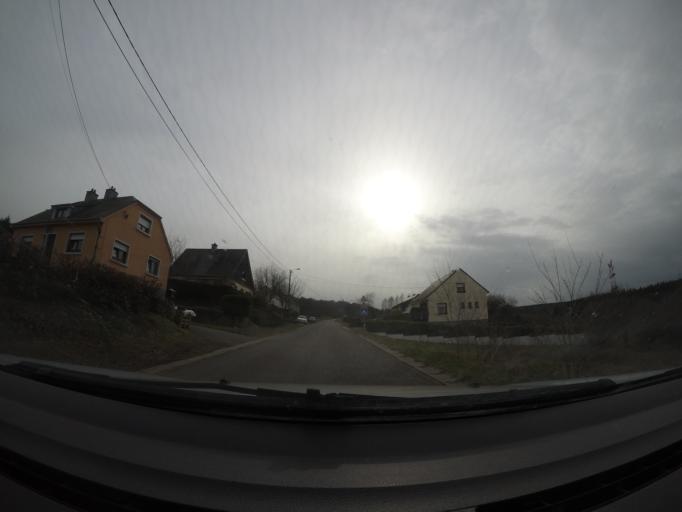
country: BE
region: Wallonia
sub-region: Province du Luxembourg
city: Martelange
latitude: 49.8258
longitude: 5.7260
